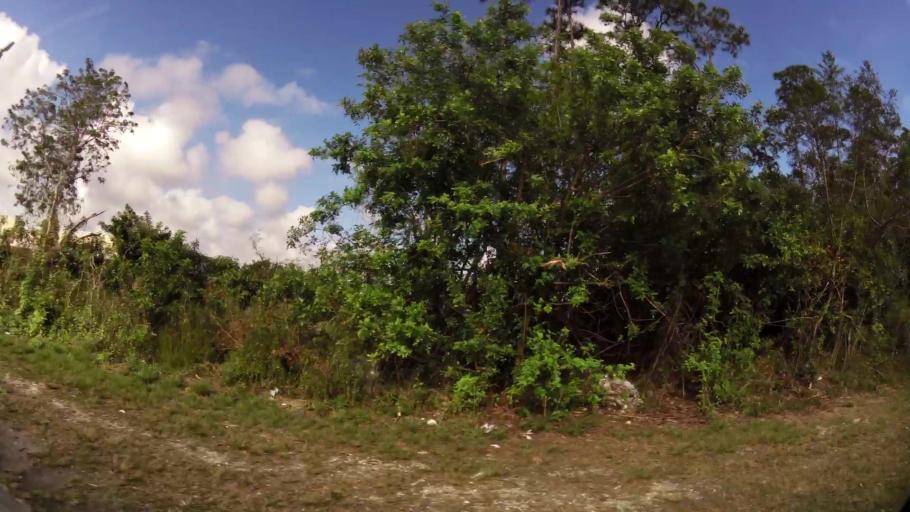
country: BS
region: Freeport
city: Lucaya
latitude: 26.5258
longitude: -78.6732
